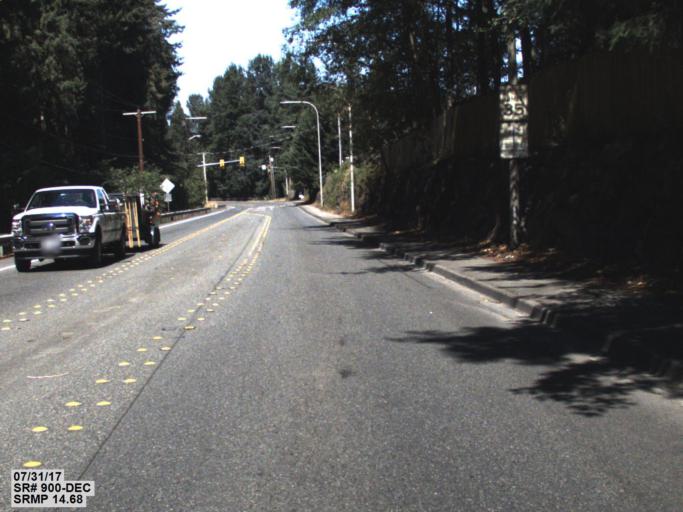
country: US
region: Washington
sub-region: King County
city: Newcastle
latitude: 47.5052
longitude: -122.1495
